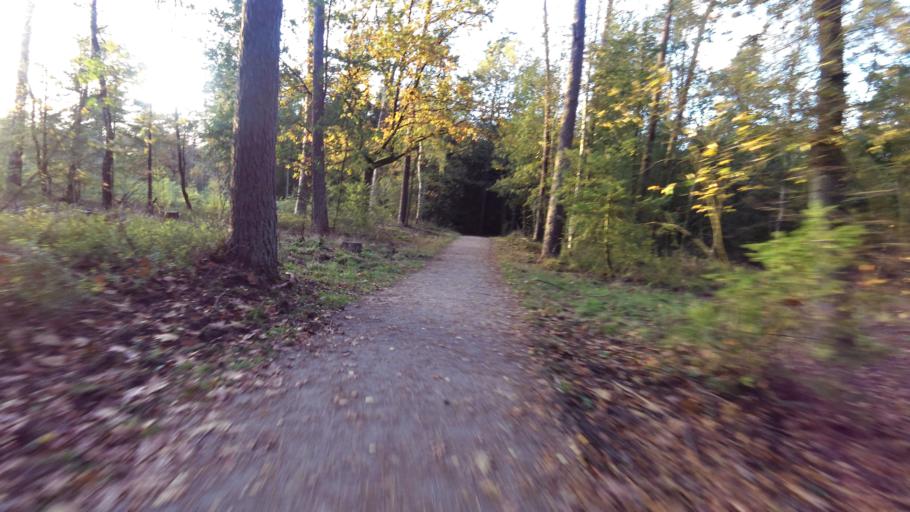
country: NL
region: Gelderland
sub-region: Gemeente Epe
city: Epe
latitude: 52.3708
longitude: 5.9623
